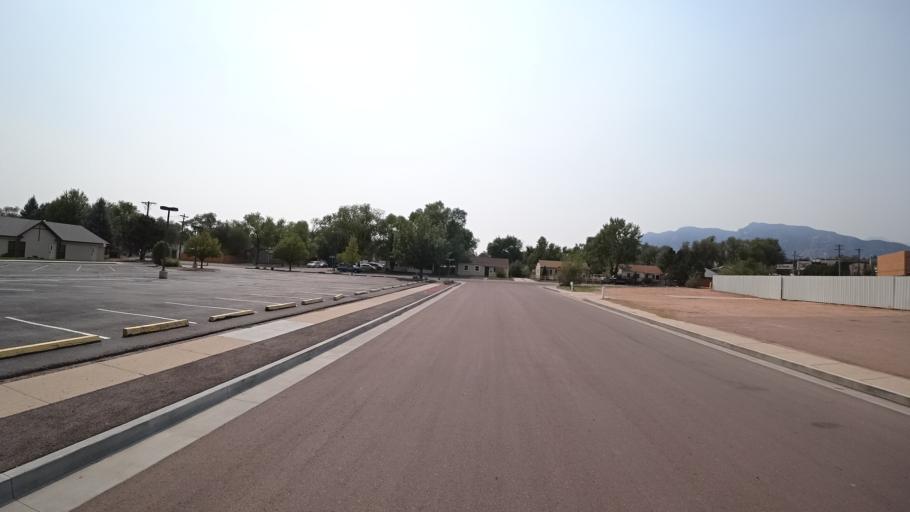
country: US
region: Colorado
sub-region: El Paso County
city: Colorado Springs
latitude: 38.8074
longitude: -104.8190
